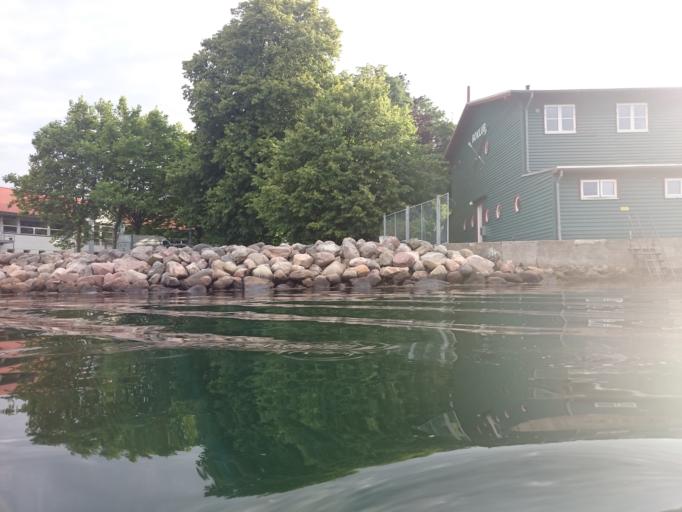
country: DK
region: South Denmark
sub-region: Svendborg Kommune
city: Svendborg
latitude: 55.0596
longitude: 10.6230
